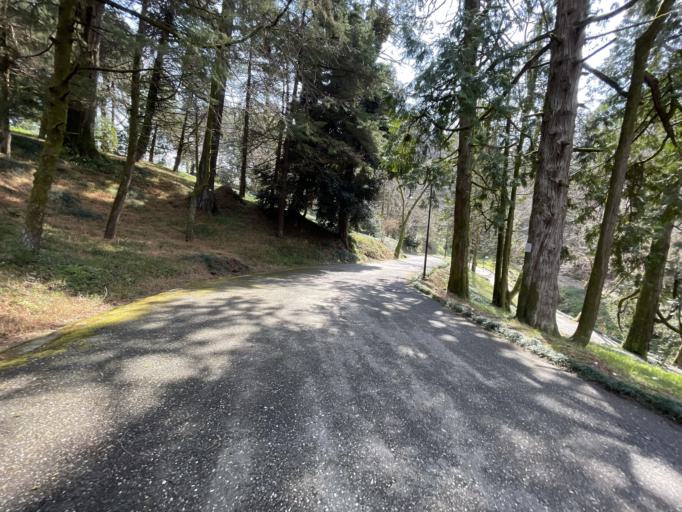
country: GE
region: Ajaria
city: Makhinjauri
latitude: 41.7041
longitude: 41.7212
